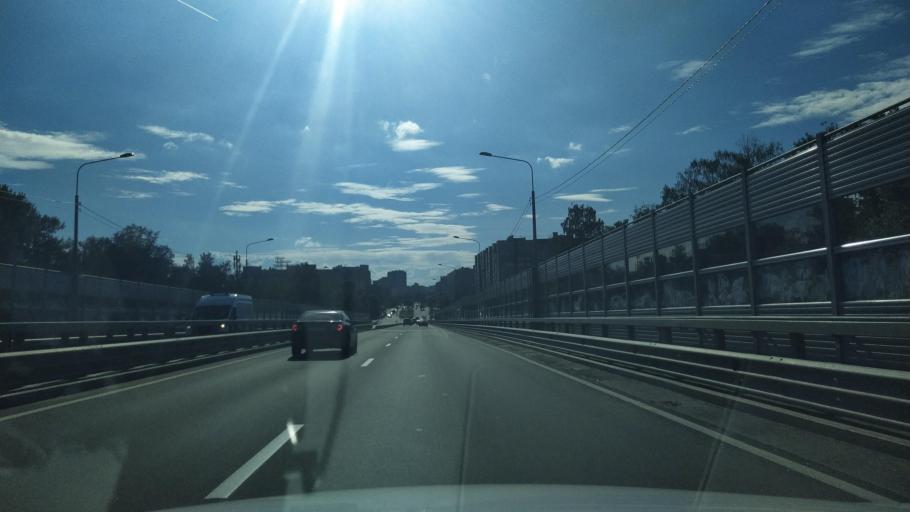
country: RU
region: St.-Petersburg
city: Ozerki
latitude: 60.0261
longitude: 30.3073
